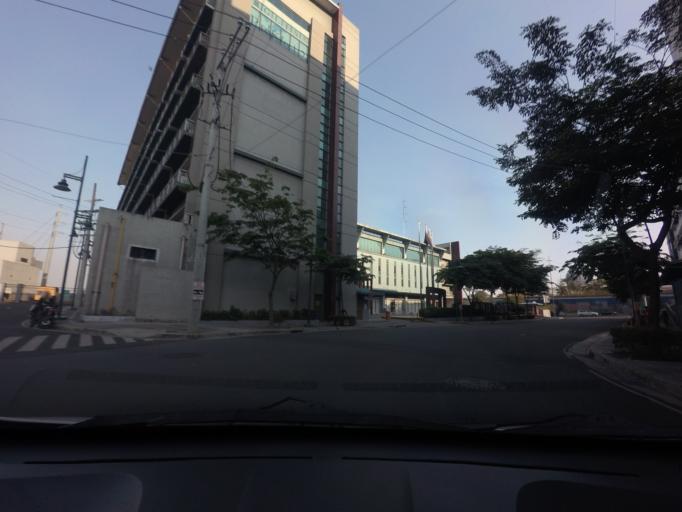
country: PH
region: Calabarzon
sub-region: Province of Rizal
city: Pateros
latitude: 14.5522
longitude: 121.0585
